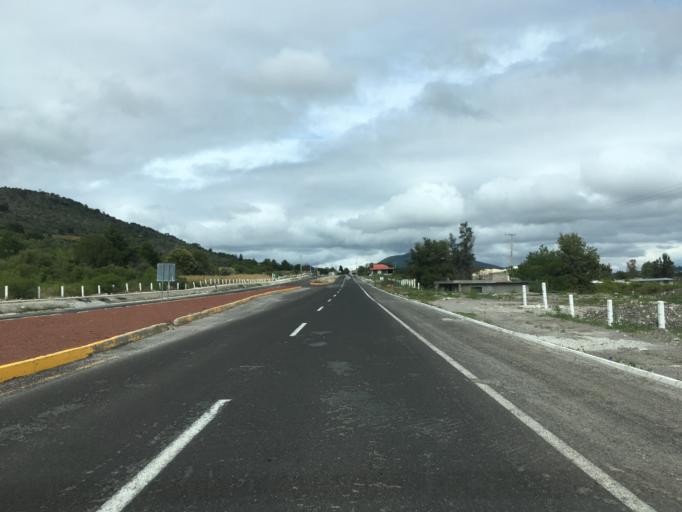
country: MX
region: Hidalgo
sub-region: Atotonilco el Grande
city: Santa Maria Amajac
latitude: 20.3577
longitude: -98.7182
